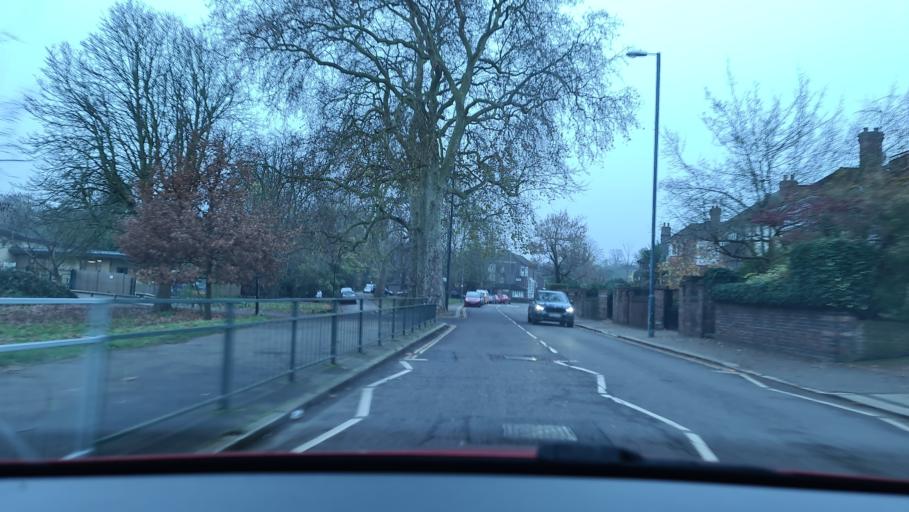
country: GB
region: England
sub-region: Greater London
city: Richmond
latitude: 51.4593
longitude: -0.2892
